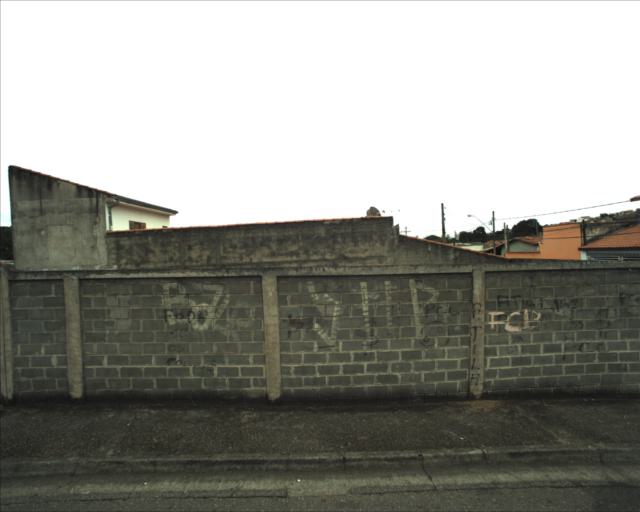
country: BR
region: Sao Paulo
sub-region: Sorocaba
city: Sorocaba
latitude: -23.5144
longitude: -47.4396
